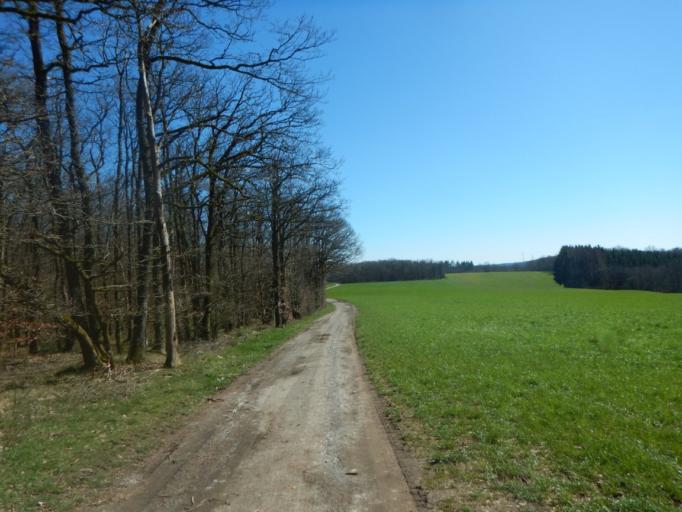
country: LU
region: Diekirch
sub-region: Canton de Wiltz
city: Eschweiler
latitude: 49.9908
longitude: 5.9307
